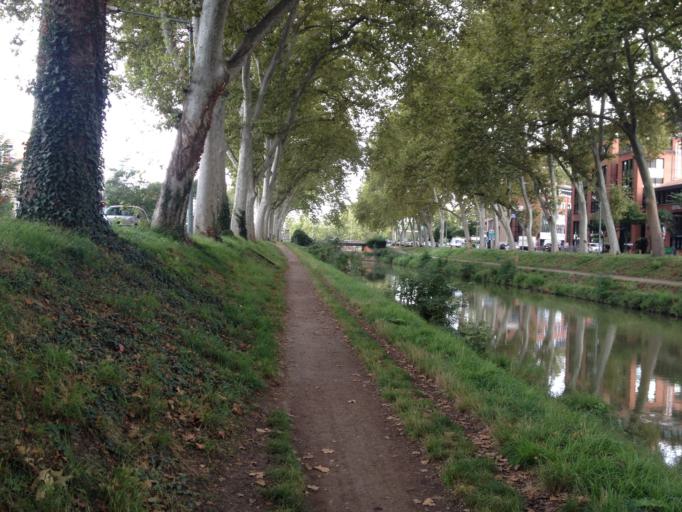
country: FR
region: Midi-Pyrenees
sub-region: Departement de la Haute-Garonne
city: Toulouse
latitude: 43.6096
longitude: 1.4213
